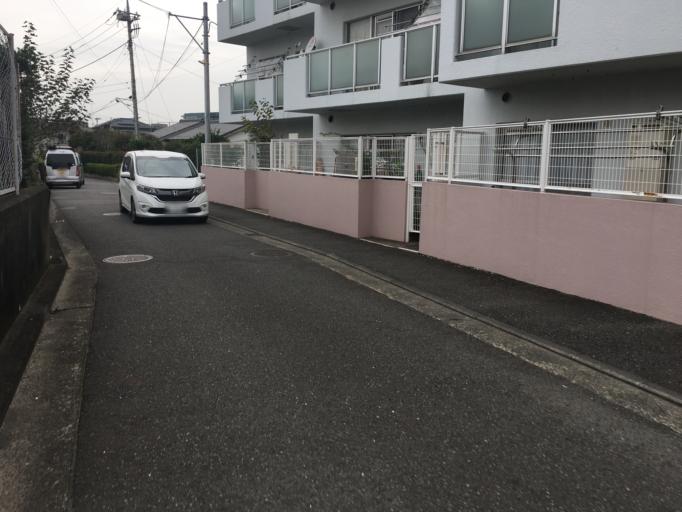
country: JP
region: Tokyo
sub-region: Machida-shi
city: Machida
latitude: 35.5140
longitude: 139.5466
